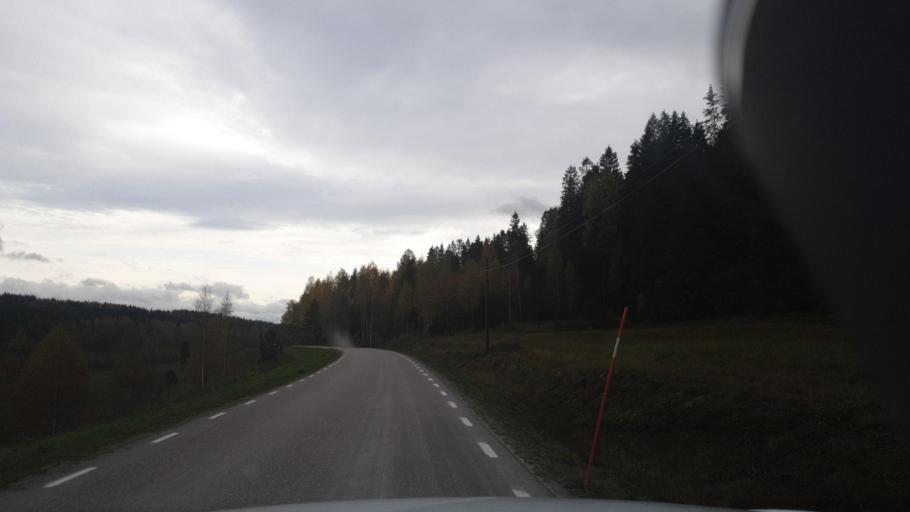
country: SE
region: Vaermland
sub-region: Arvika Kommun
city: Arvika
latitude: 59.7826
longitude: 12.7694
